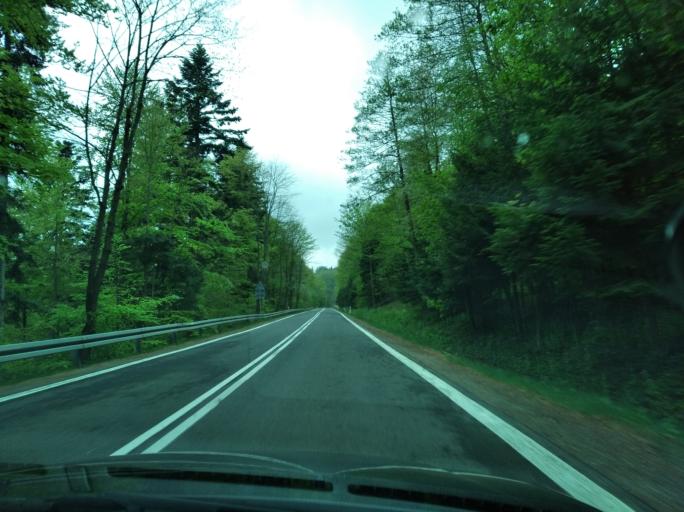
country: PL
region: Subcarpathian Voivodeship
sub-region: Powiat sanocki
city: Tyrawa Woloska
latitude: 49.5621
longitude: 22.3404
